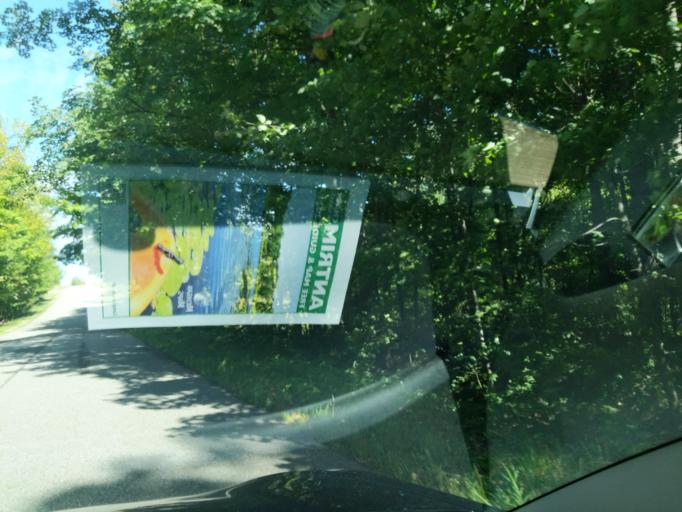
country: US
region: Michigan
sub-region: Antrim County
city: Elk Rapids
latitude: 44.9485
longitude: -85.3323
